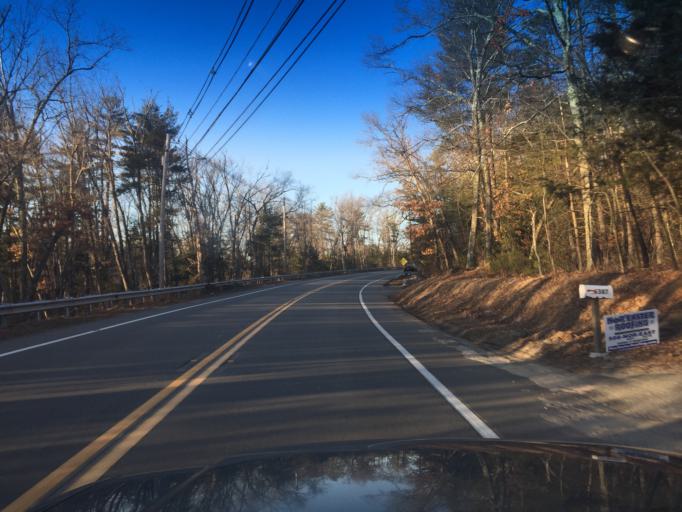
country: US
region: Massachusetts
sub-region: Worcester County
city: Uxbridge
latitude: 42.0857
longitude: -71.6062
